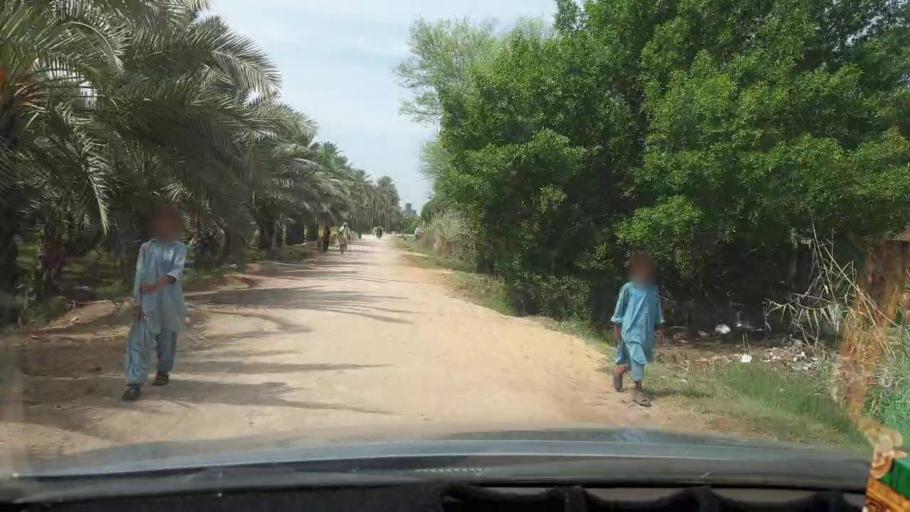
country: PK
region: Sindh
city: Khairpur
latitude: 27.4890
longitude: 68.7534
